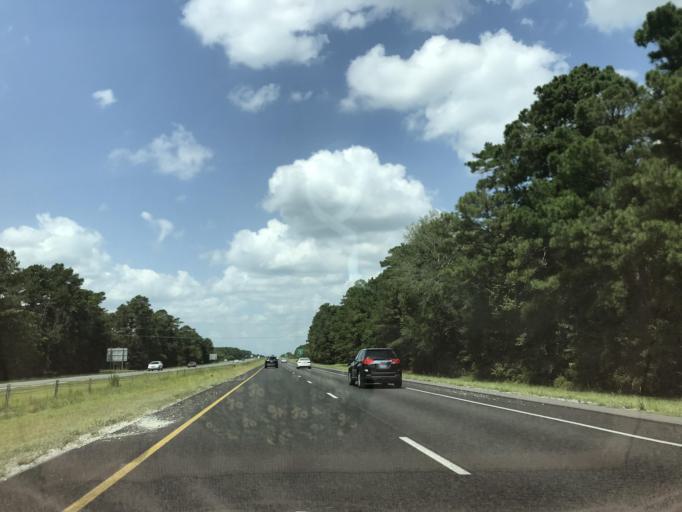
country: US
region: North Carolina
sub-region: Duplin County
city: Wallace
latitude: 34.7639
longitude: -77.9592
